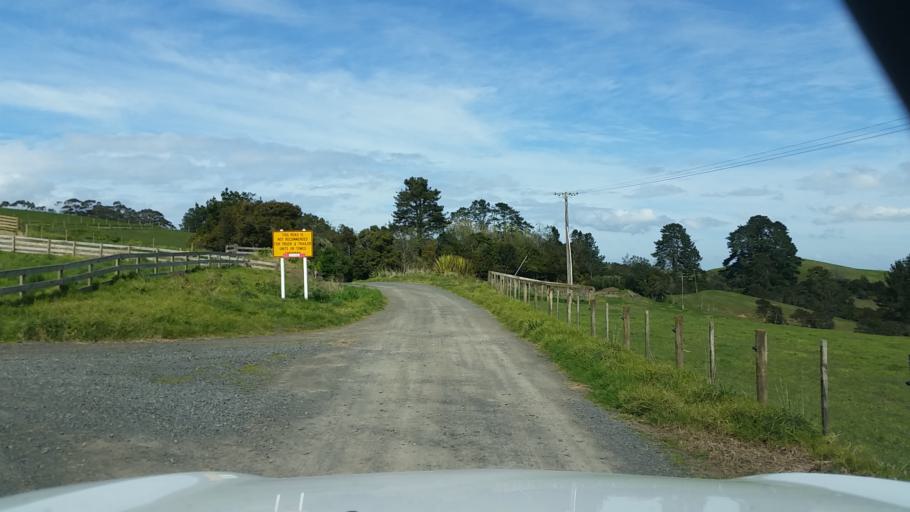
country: NZ
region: Waikato
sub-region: Hauraki District
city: Ngatea
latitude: -37.4588
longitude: 175.4692
